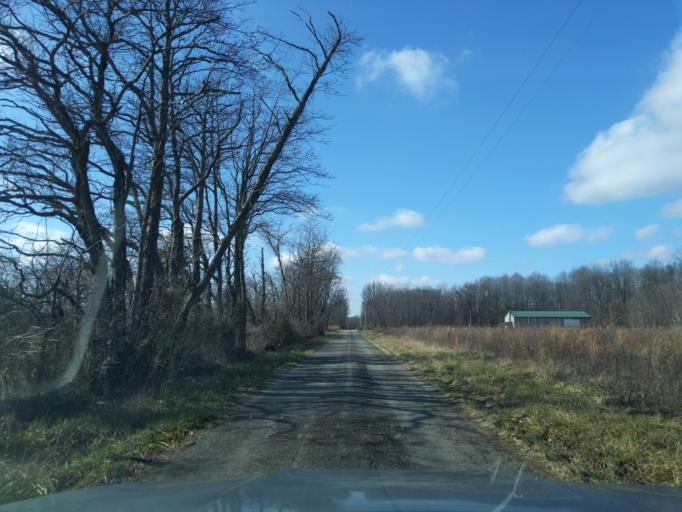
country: US
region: Indiana
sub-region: Decatur County
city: Greensburg
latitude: 39.2409
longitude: -85.4515
